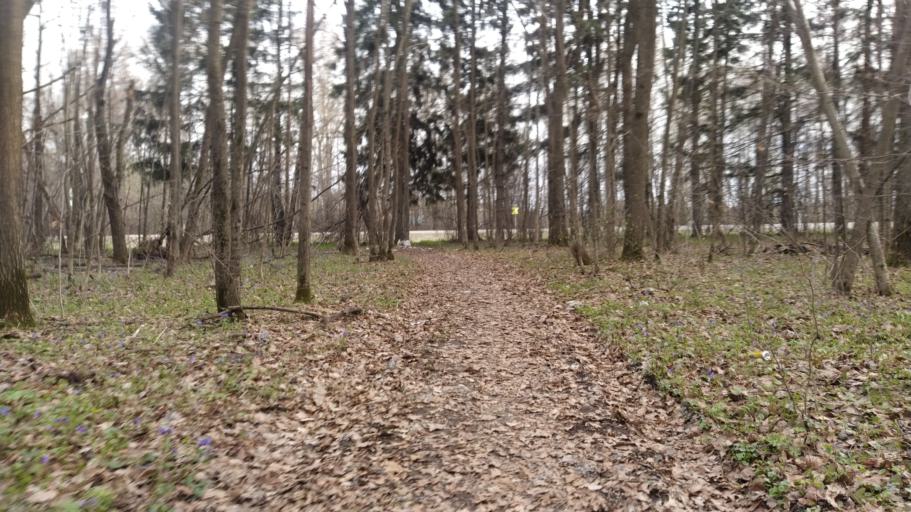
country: RU
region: Chuvashia
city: Novyye Lapsary
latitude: 56.1285
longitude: 47.1219
